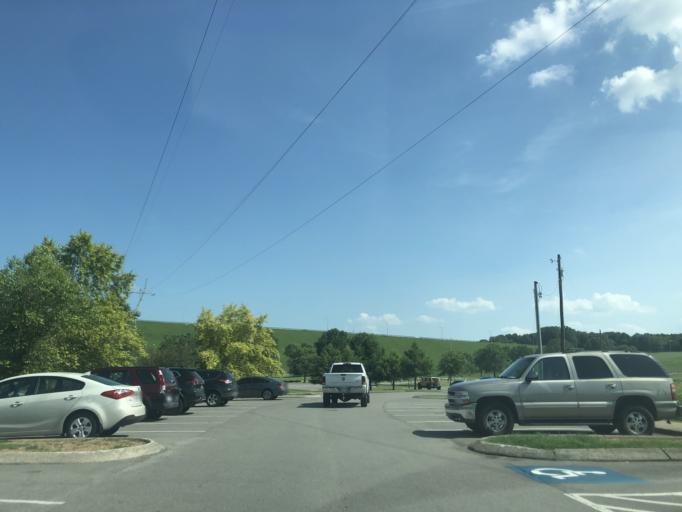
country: US
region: Tennessee
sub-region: Davidson County
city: Lakewood
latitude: 36.1585
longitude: -86.6212
